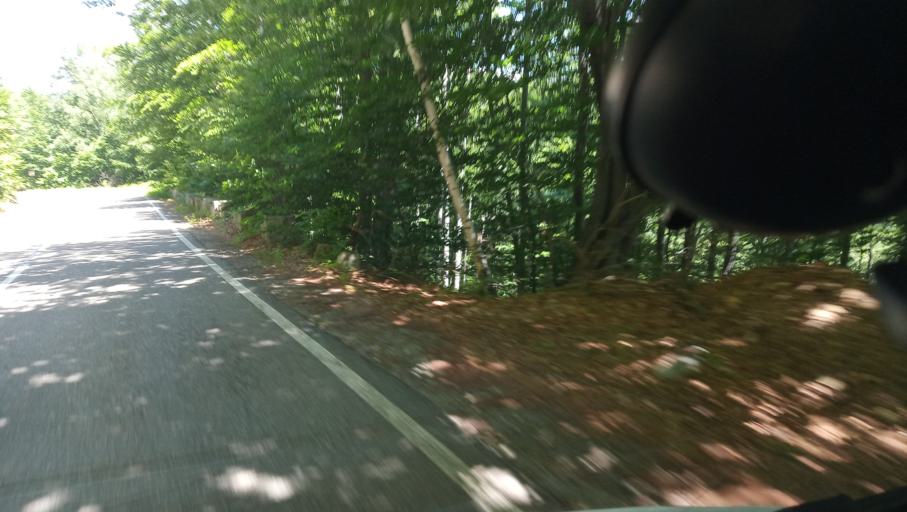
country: RO
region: Mehedinti
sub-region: Comuna Isverna
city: Isverna
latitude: 45.0388
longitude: 22.6170
